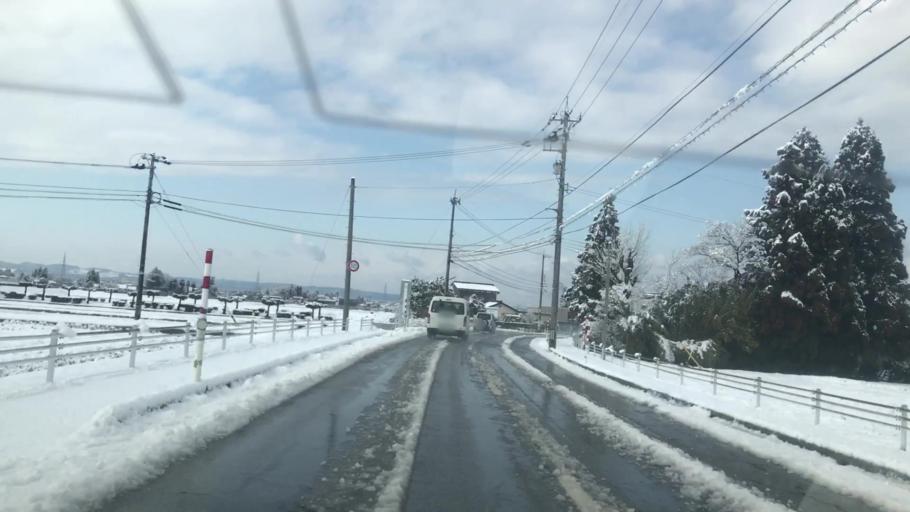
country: JP
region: Toyama
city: Toyama-shi
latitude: 36.6276
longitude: 137.2390
